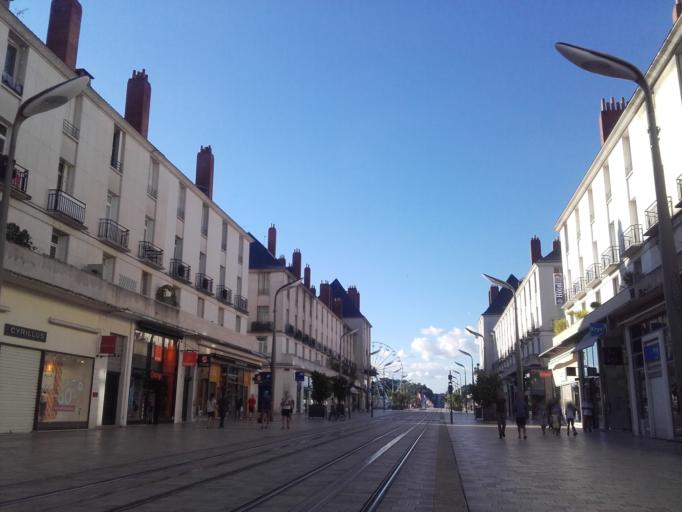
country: FR
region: Centre
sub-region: Departement d'Indre-et-Loire
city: Tours
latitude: 47.3942
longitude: 0.6872
